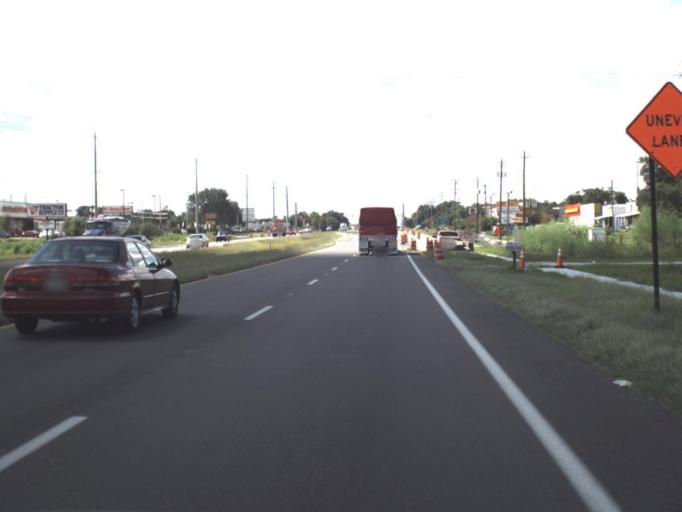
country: US
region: Florida
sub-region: Polk County
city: Gibsonia
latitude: 28.1323
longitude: -81.9738
